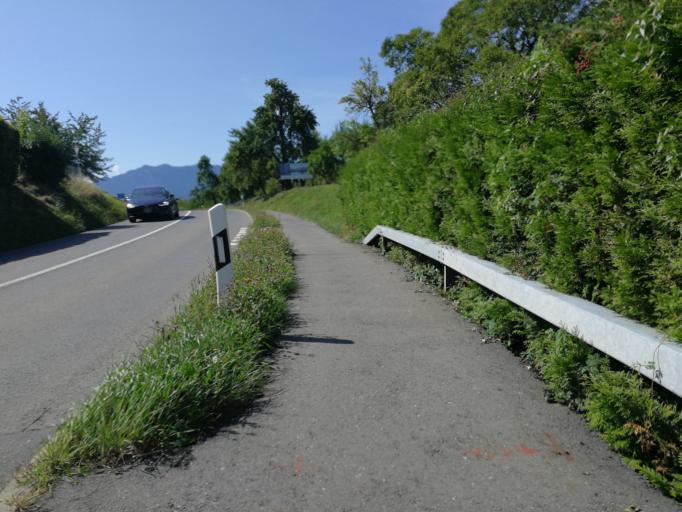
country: CH
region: Lucerne
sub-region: Lucerne-Land District
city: Weggis
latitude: 47.0500
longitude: 8.4267
